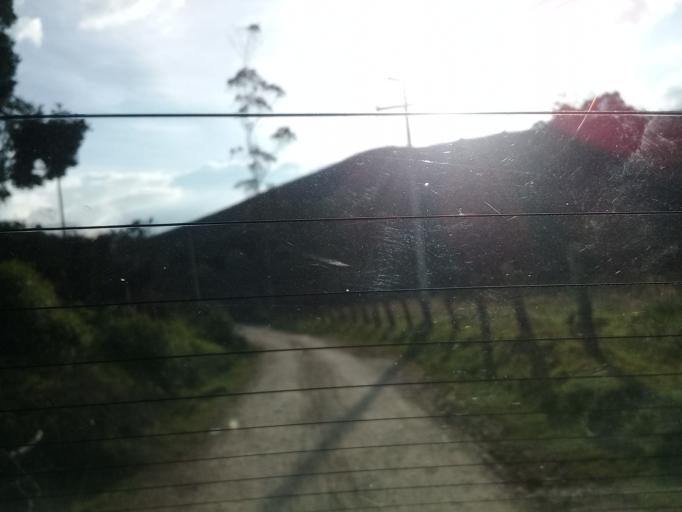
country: CO
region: Cundinamarca
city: Sibate
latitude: 4.4373
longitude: -74.2810
